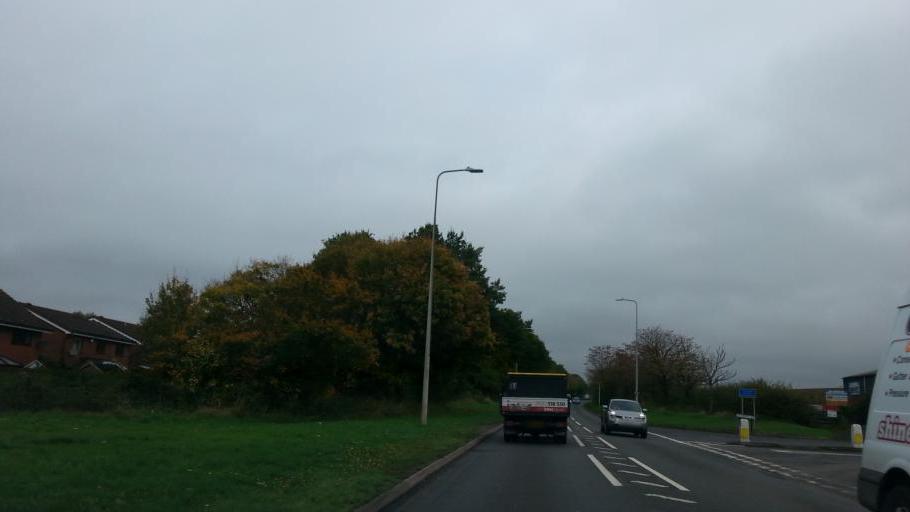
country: GB
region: England
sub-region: Worcestershire
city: Bromsgrove
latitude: 52.3425
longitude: -2.0484
